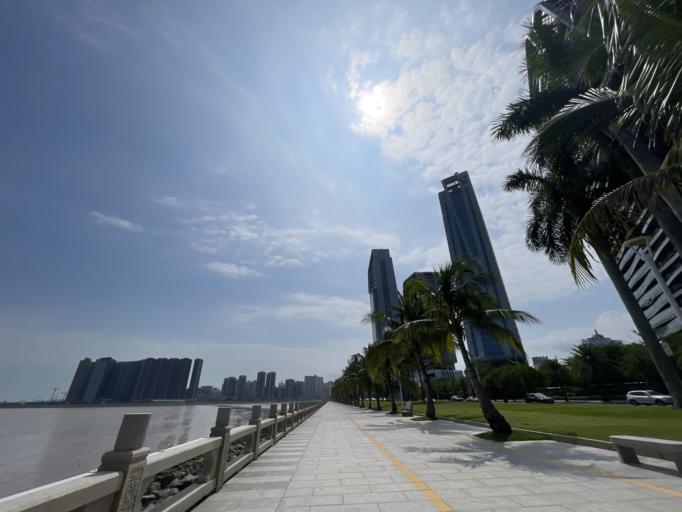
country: MO
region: Macau
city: Macau
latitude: 22.2247
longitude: 113.5561
